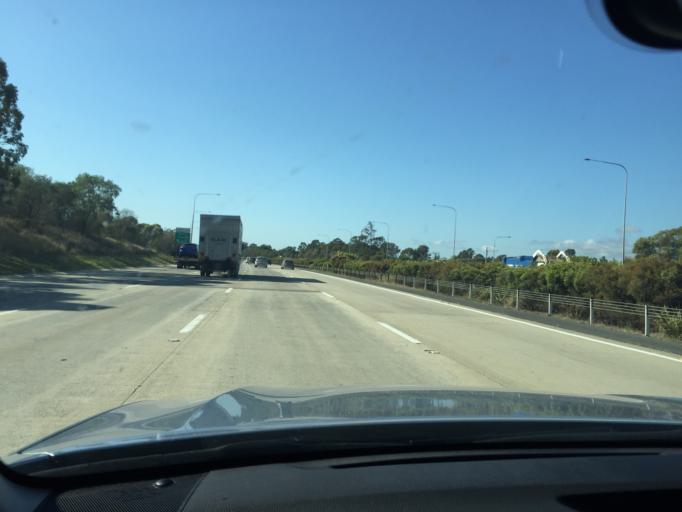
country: AU
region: Queensland
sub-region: Gold Coast
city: Yatala
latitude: -27.7541
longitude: 153.2382
